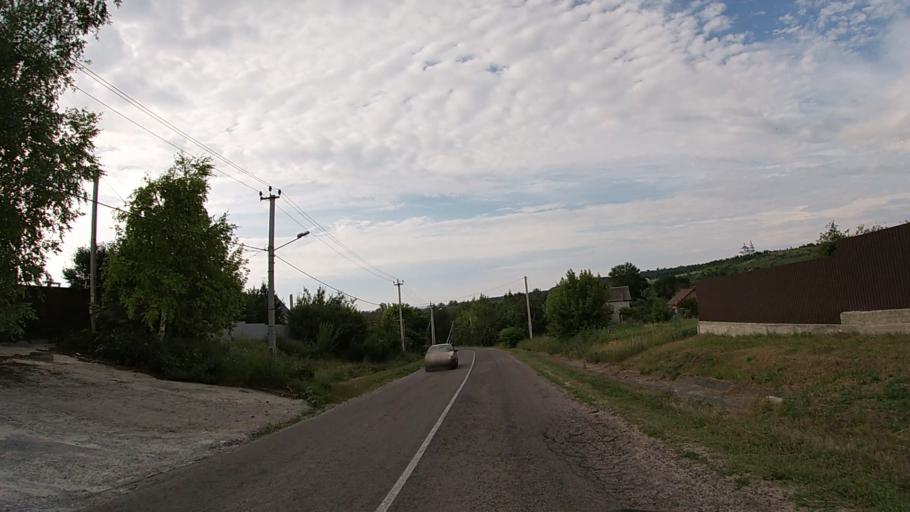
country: RU
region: Belgorod
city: Severnyy
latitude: 50.7131
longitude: 36.5957
